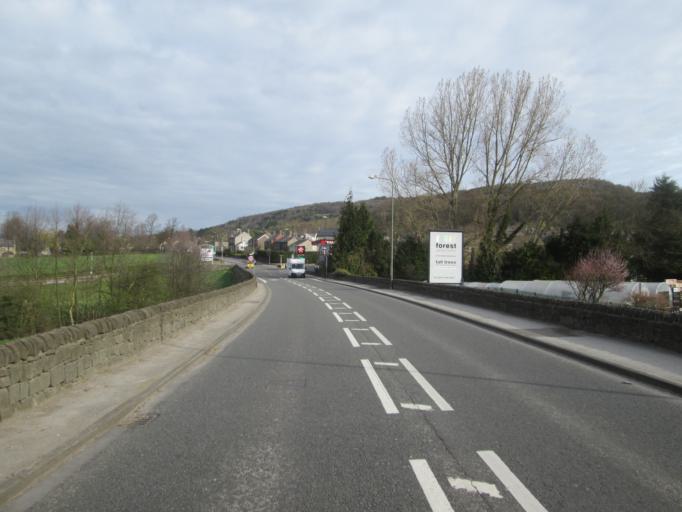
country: GB
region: England
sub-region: Derbyshire
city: Matlock
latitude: 53.1598
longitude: -1.5867
